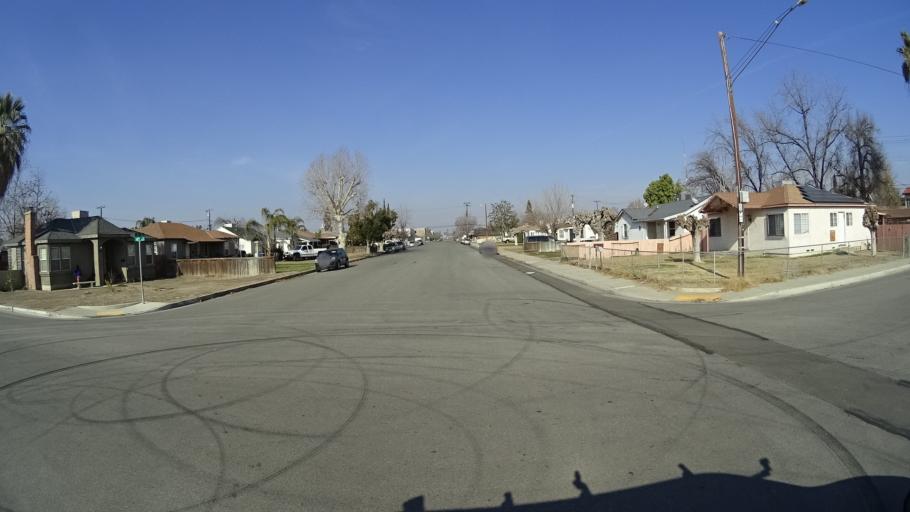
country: US
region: California
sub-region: Kern County
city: Bakersfield
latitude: 35.3664
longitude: -119.0084
